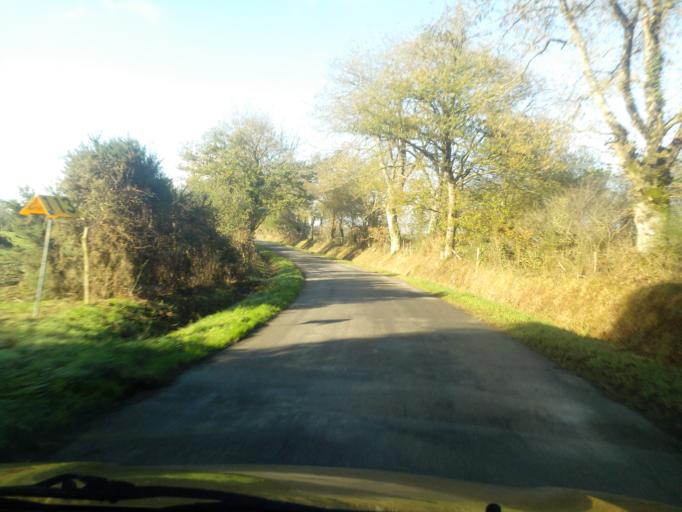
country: FR
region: Brittany
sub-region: Departement du Morbihan
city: Pleucadeuc
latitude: 47.7268
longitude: -2.3844
